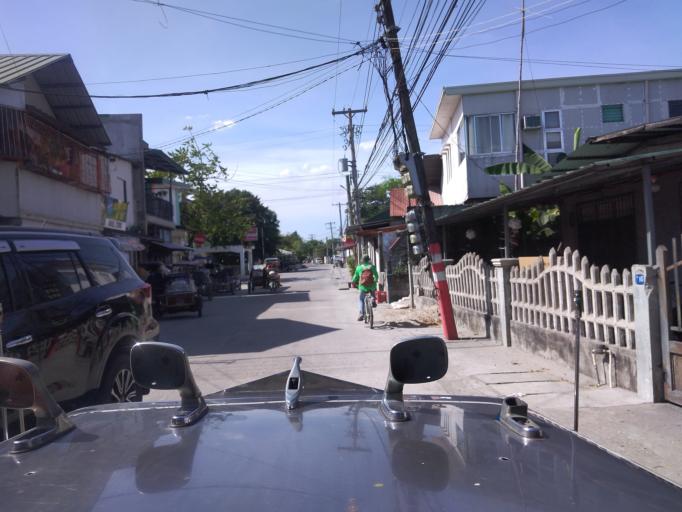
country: PH
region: Central Luzon
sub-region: Province of Pampanga
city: Magliman
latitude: 15.0347
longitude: 120.6652
